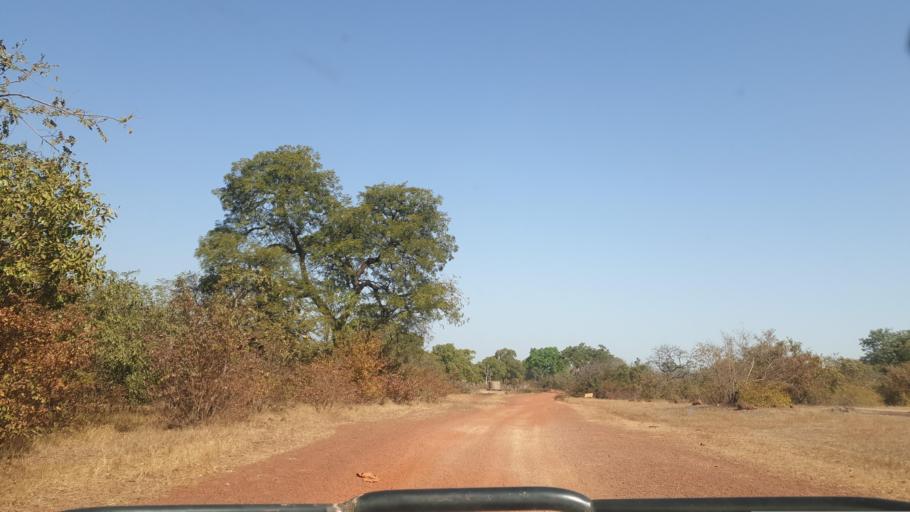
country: ML
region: Sikasso
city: Bougouni
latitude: 11.8334
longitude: -6.9787
